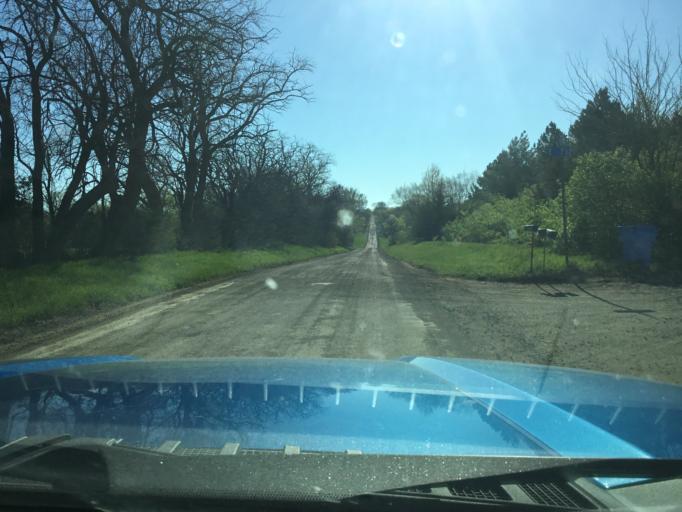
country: US
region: Kansas
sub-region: Douglas County
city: Lawrence
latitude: 38.9569
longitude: -95.3666
